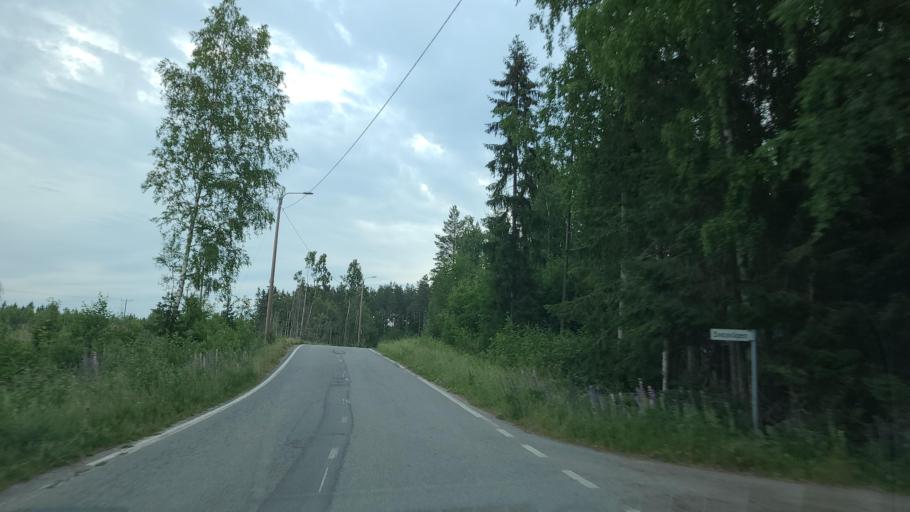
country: FI
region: Ostrobothnia
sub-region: Vaasa
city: Replot
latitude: 63.1689
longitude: 21.2623
